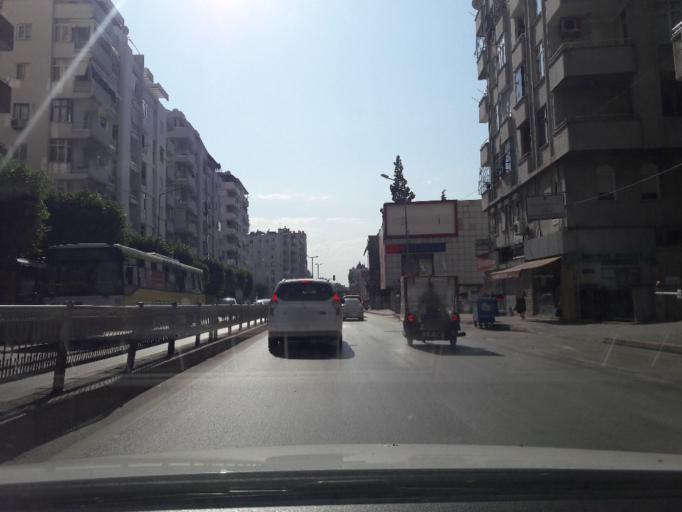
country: TR
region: Adana
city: Adana
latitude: 37.0107
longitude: 35.3234
